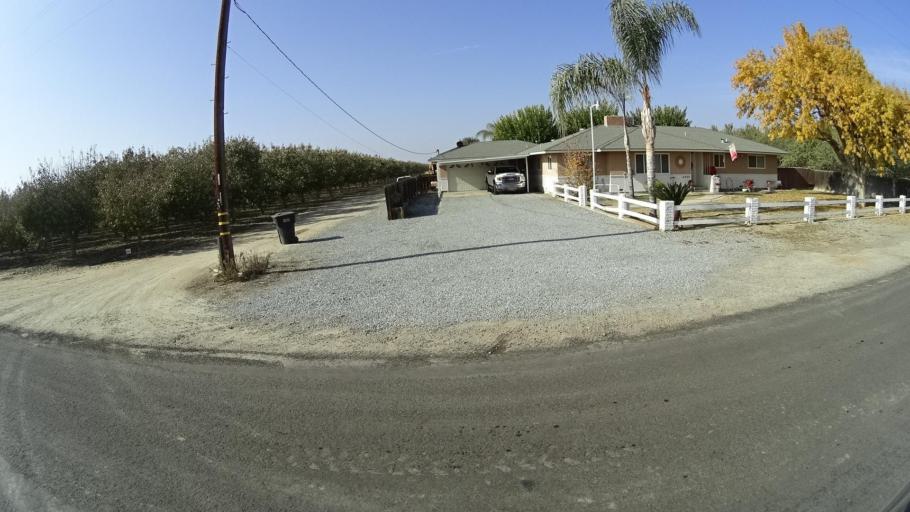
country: US
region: California
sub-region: Kern County
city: McFarland
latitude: 35.6420
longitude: -119.1867
